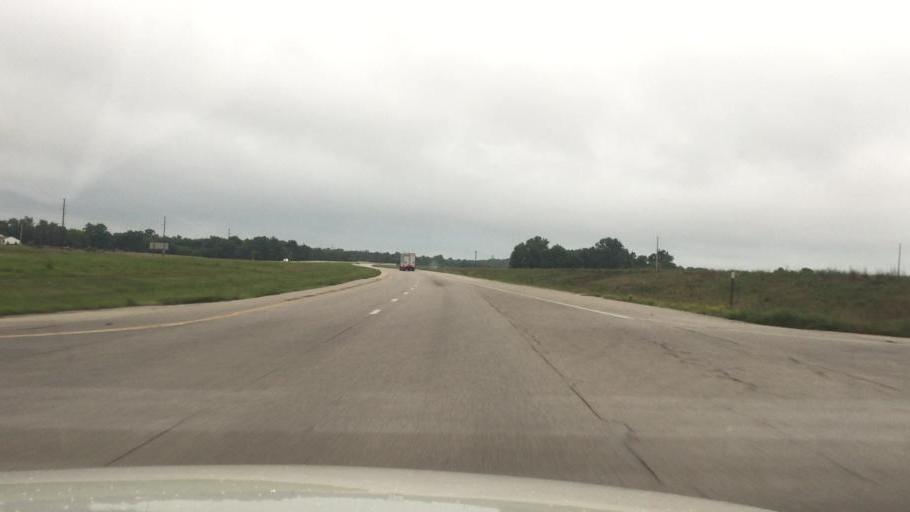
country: US
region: Kansas
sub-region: Montgomery County
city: Coffeyville
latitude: 37.0741
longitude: -95.5883
